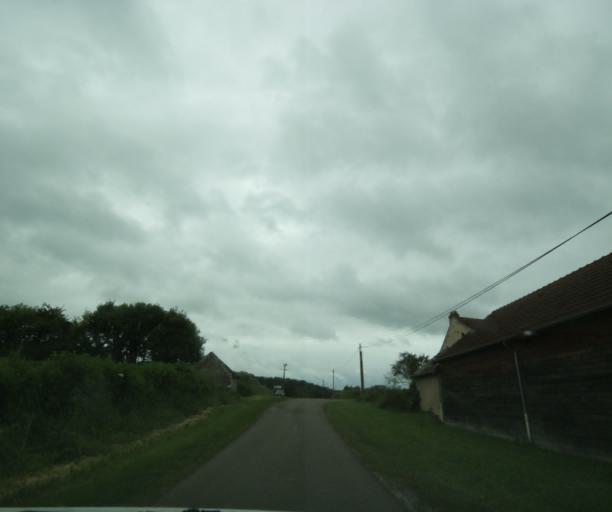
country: FR
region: Bourgogne
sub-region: Departement de Saone-et-Loire
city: Charolles
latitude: 46.4814
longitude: 4.2735
